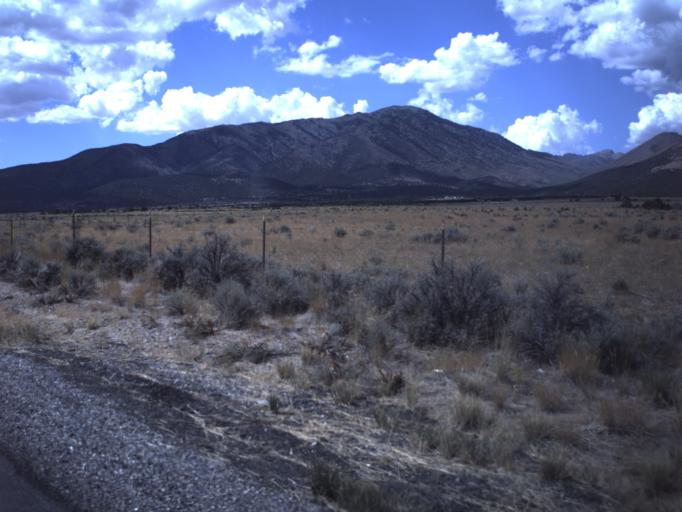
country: US
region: Utah
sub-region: Tooele County
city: Grantsville
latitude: 40.3361
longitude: -112.5062
